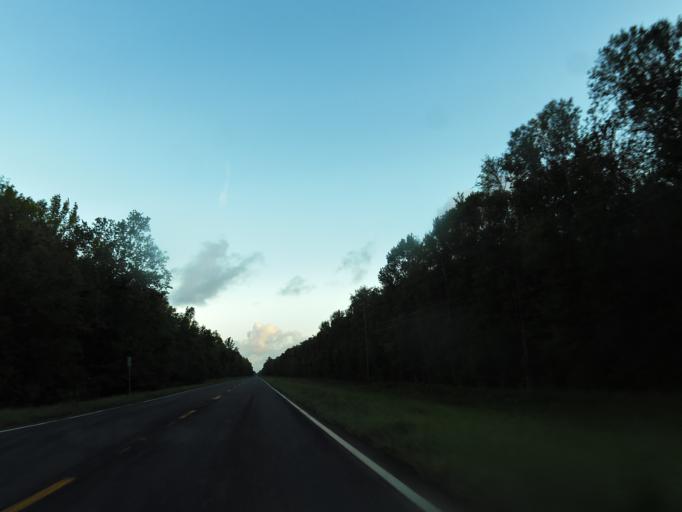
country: US
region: Georgia
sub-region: Camden County
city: Woodbine
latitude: 30.8994
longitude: -81.7099
